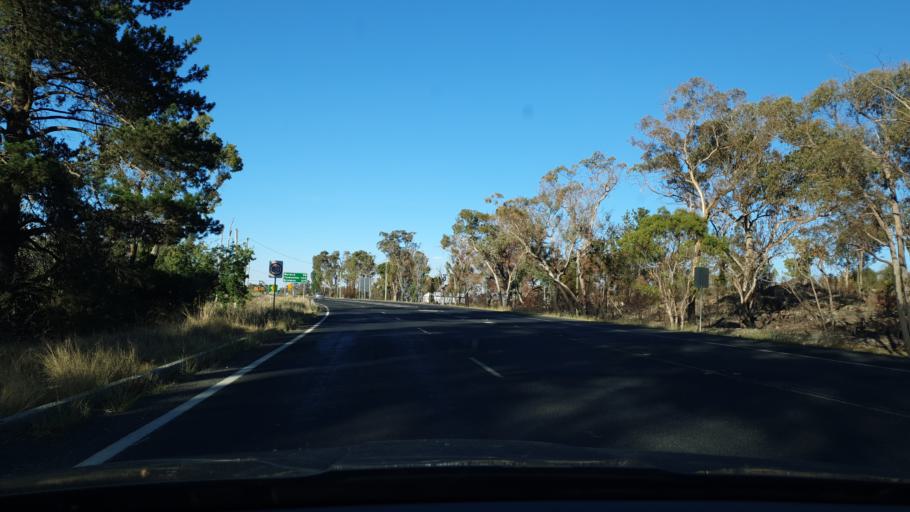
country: AU
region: Queensland
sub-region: Southern Downs
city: Stanthorpe
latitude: -28.6345
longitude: 151.9525
